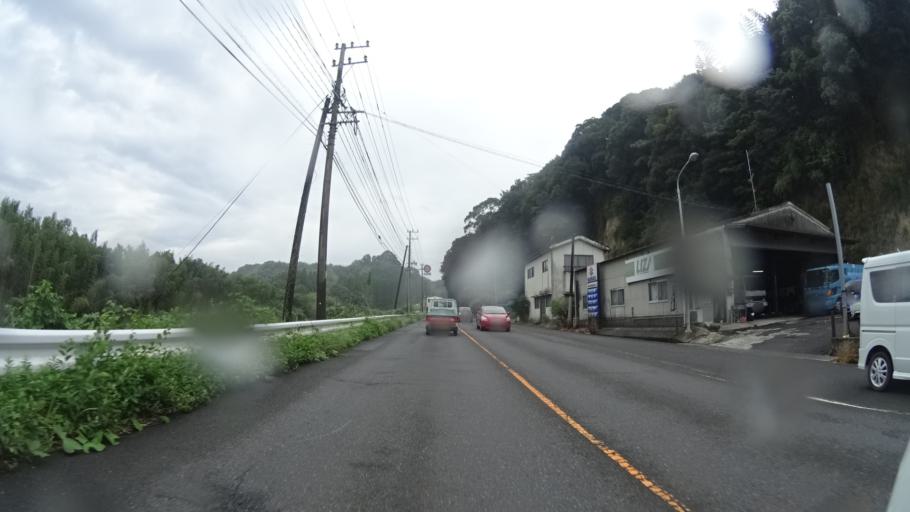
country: JP
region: Kagoshima
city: Kajiki
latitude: 31.7683
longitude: 130.6704
